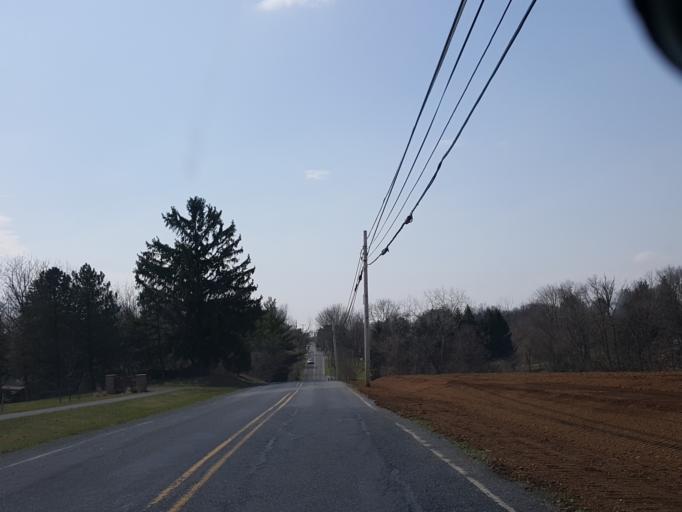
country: US
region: Pennsylvania
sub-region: Lebanon County
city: Annville
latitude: 40.3173
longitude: -76.5133
